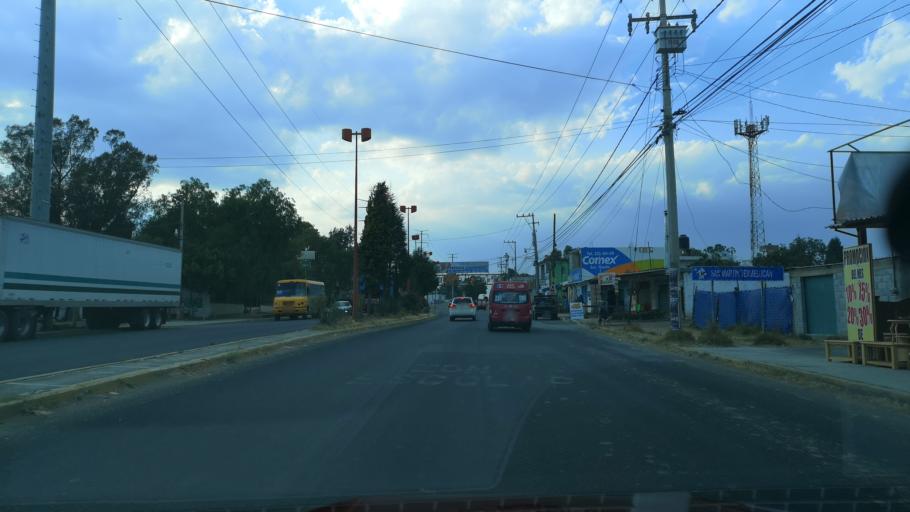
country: MX
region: Puebla
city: Cuanala
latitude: 19.0968
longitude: -98.3419
